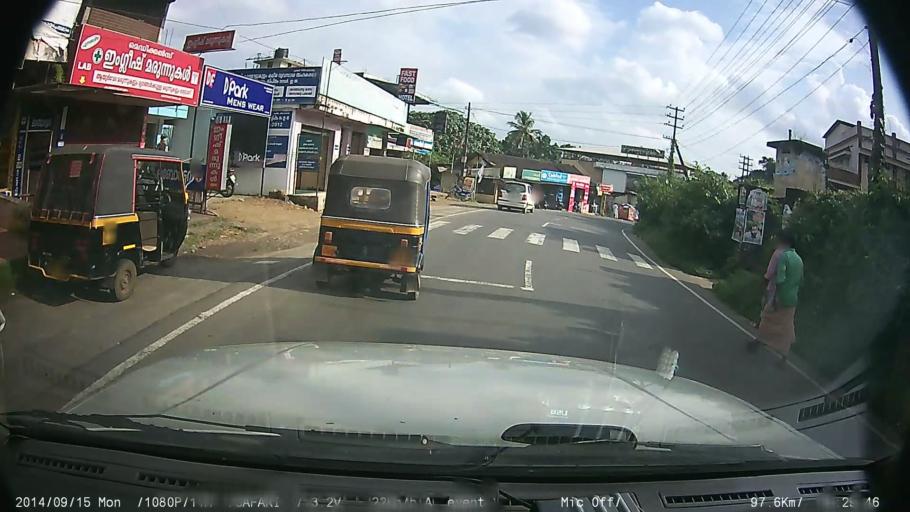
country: IN
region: Kerala
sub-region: Ernakulam
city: Piravam
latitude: 9.8646
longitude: 76.5967
